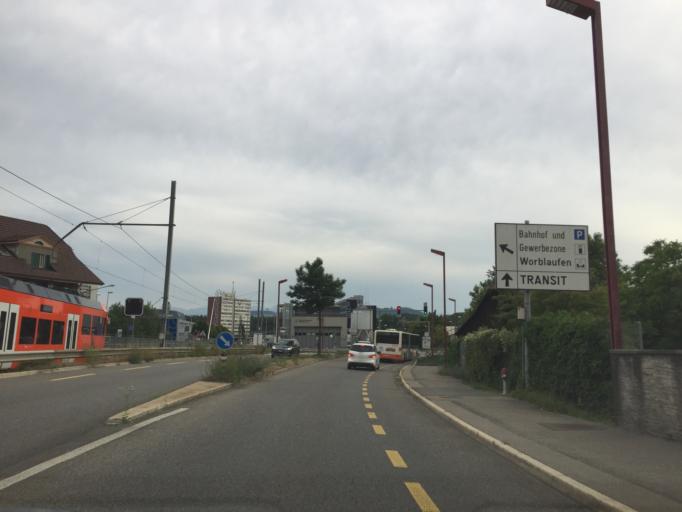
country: CH
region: Bern
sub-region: Bern-Mittelland District
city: Zollikofen
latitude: 46.9838
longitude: 7.4573
